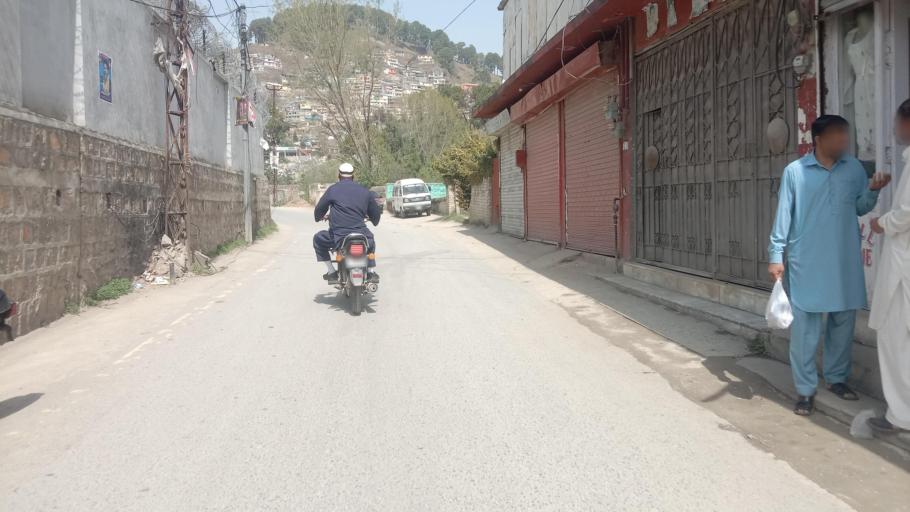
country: PK
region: Khyber Pakhtunkhwa
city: Abbottabad
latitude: 34.1475
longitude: 73.2029
